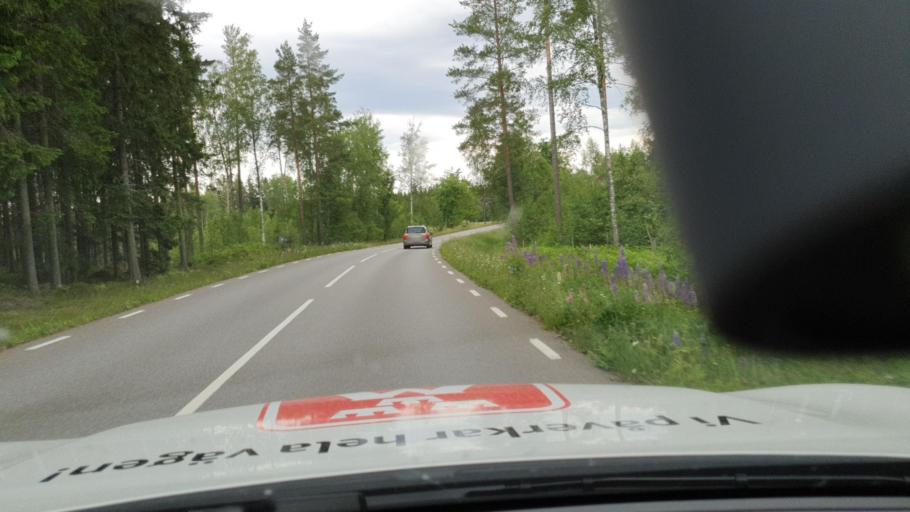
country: SE
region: Vaestra Goetaland
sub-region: Karlsborgs Kommun
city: Karlsborg
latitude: 58.7451
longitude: 14.5054
